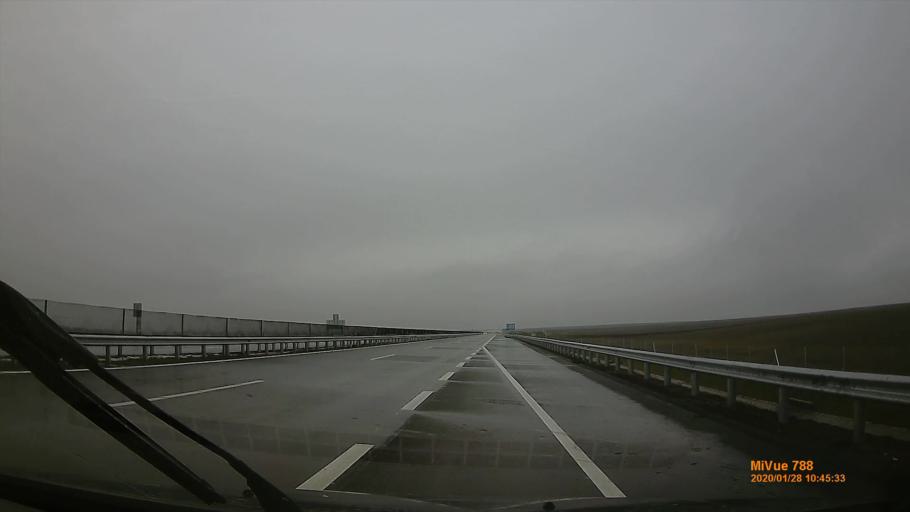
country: HU
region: Pest
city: Monor
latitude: 47.3609
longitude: 19.4840
